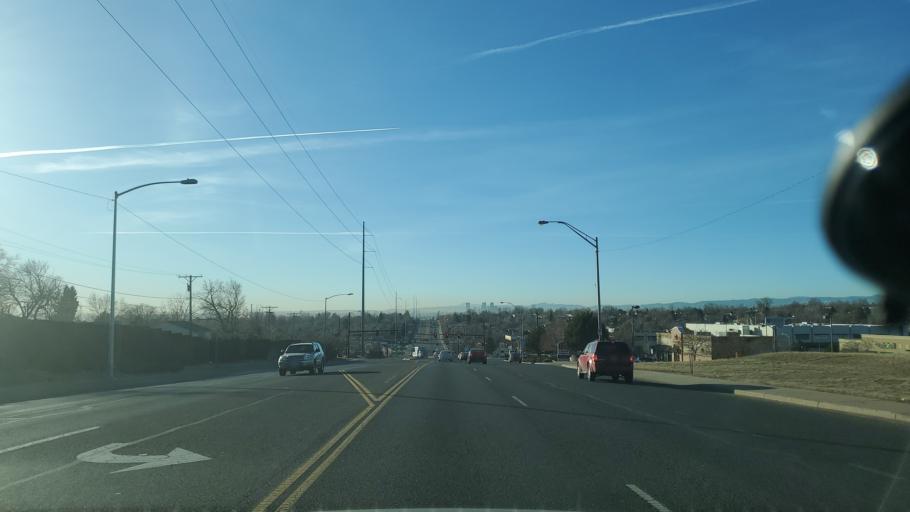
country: US
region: Colorado
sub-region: Adams County
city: Thornton
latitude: 39.8507
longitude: -104.9779
